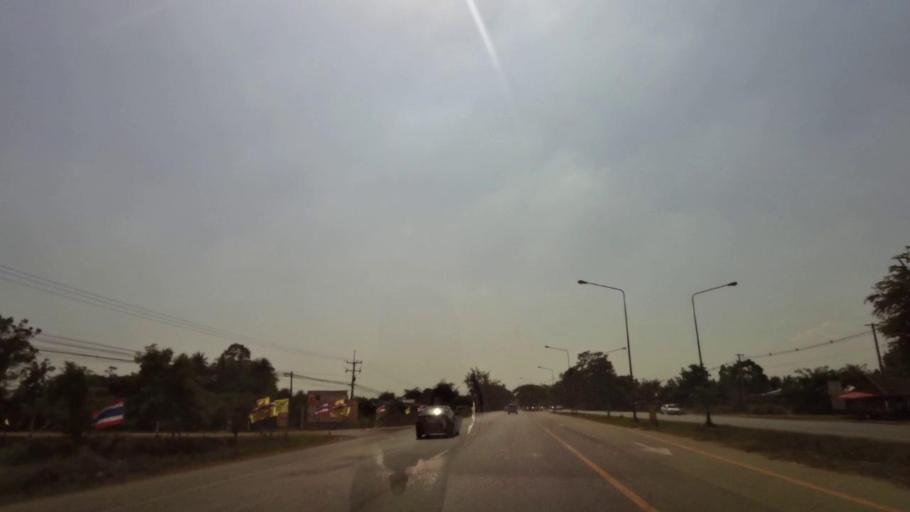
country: TH
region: Phichit
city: Wachira Barami
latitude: 16.3728
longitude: 100.1334
